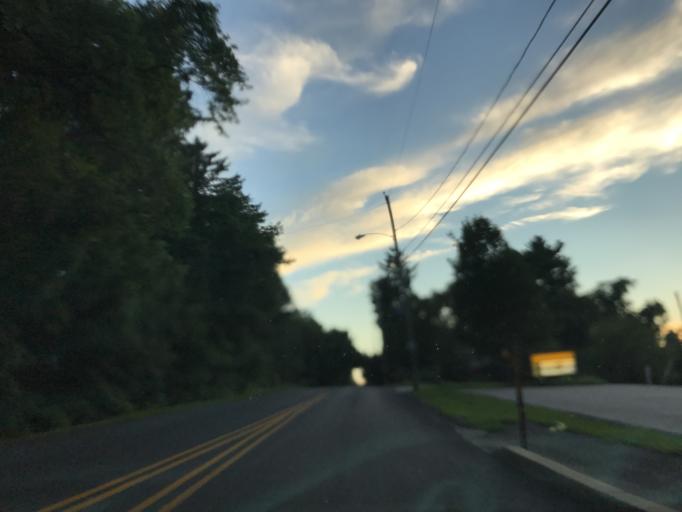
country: US
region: Pennsylvania
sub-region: York County
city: Valley View
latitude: 39.9495
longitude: -76.7059
